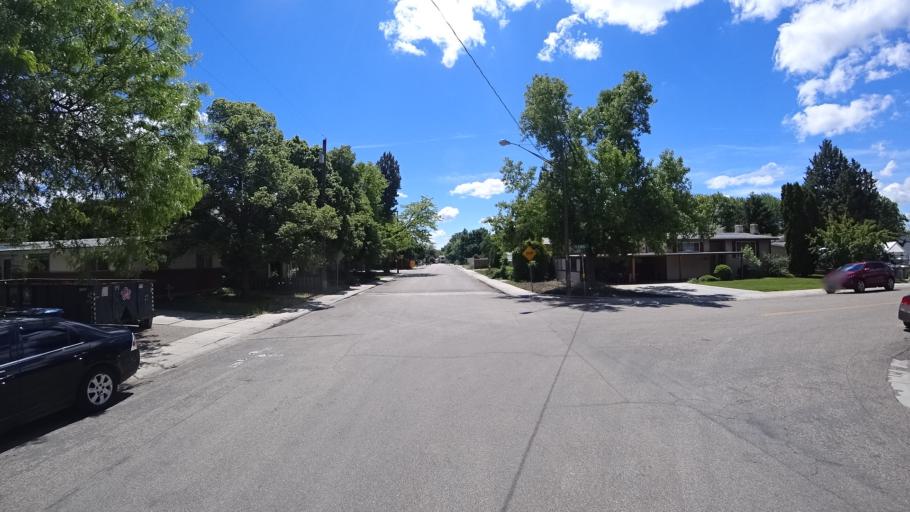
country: US
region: Idaho
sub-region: Ada County
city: Boise
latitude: 43.5772
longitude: -116.2014
